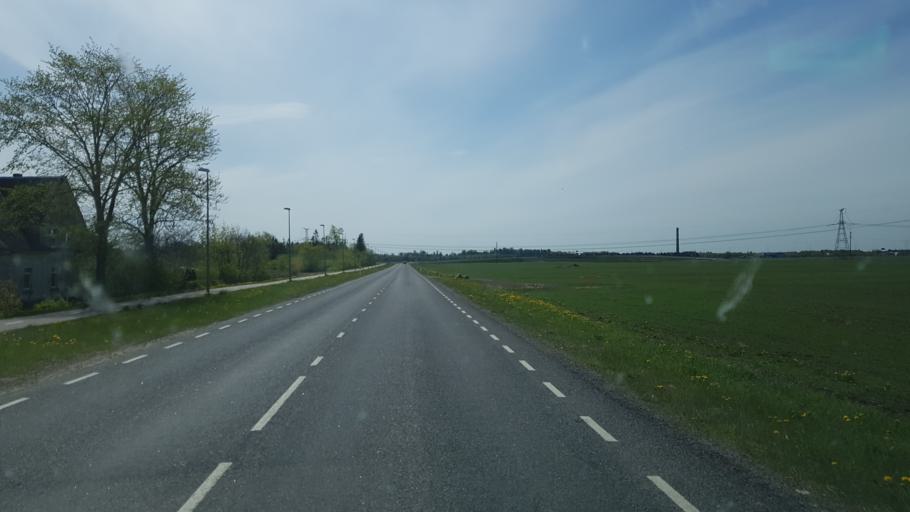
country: EE
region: Ida-Virumaa
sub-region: Kohtla-Jaerve linn
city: Kohtla-Jarve
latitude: 59.3946
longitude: 27.3438
